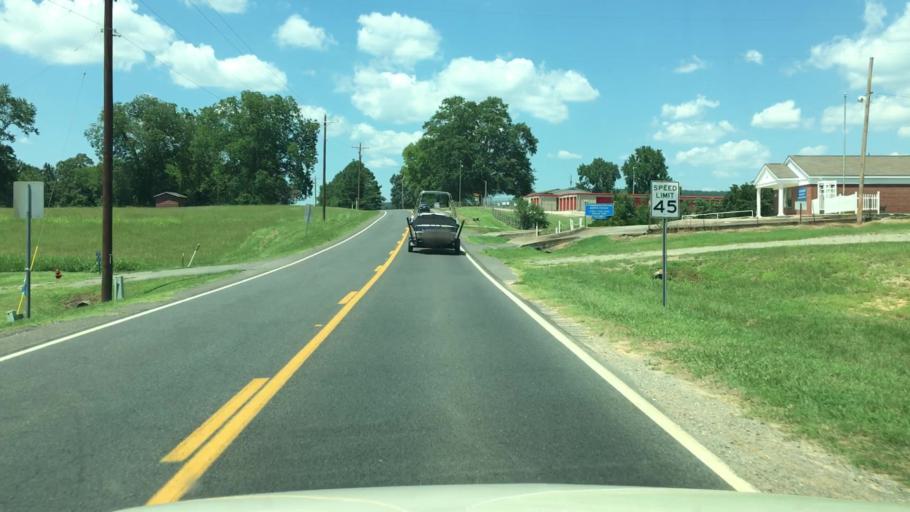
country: US
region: Arkansas
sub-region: Garland County
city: Lake Hamilton
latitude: 34.3238
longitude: -93.1730
